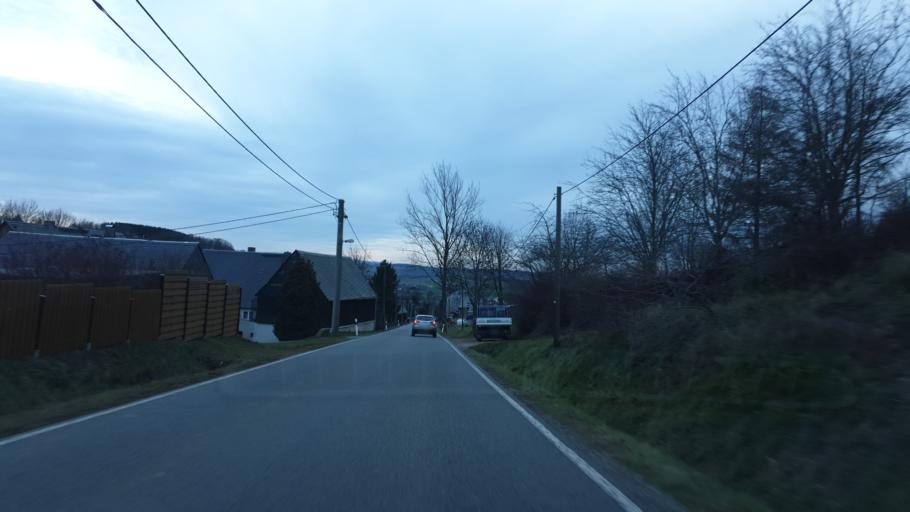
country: DE
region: Saxony
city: Hartenstein
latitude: 50.6962
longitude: 12.6765
